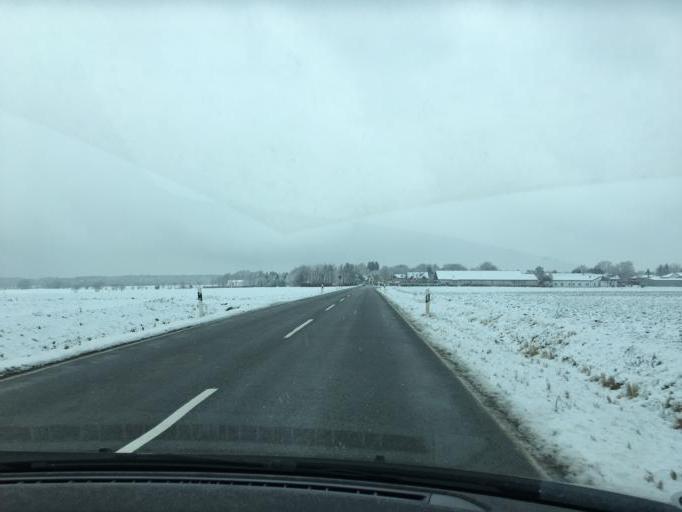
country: DE
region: North Rhine-Westphalia
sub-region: Regierungsbezirk Koln
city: Hurtgenwald
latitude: 50.7164
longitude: 6.3957
